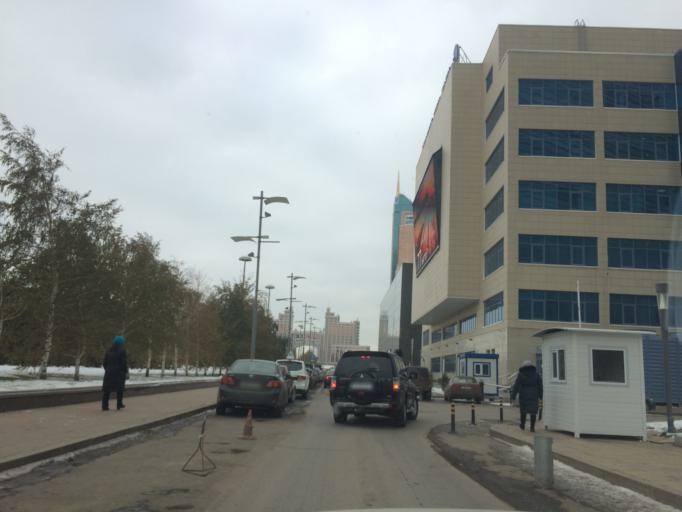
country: KZ
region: Astana Qalasy
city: Astana
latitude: 51.1301
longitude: 71.4223
